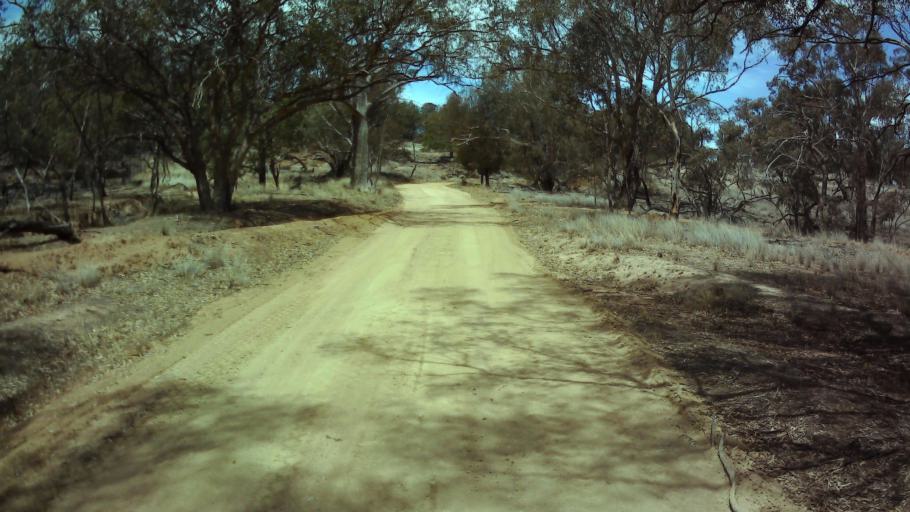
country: AU
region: New South Wales
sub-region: Weddin
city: Grenfell
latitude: -33.7864
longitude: 148.1547
